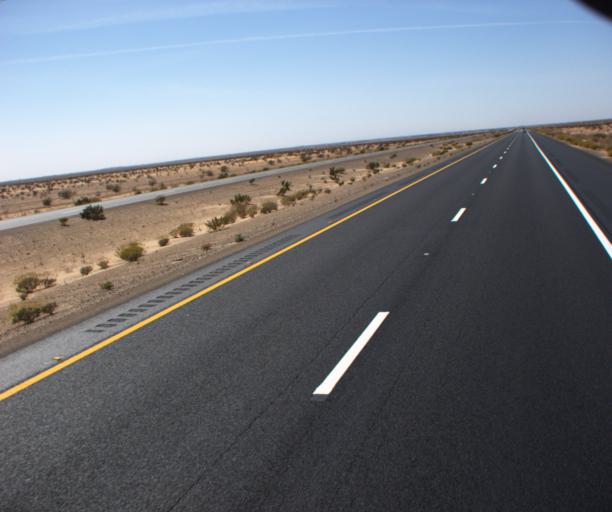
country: US
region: Arizona
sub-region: Yuma County
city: Somerton
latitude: 32.4954
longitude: -114.5896
